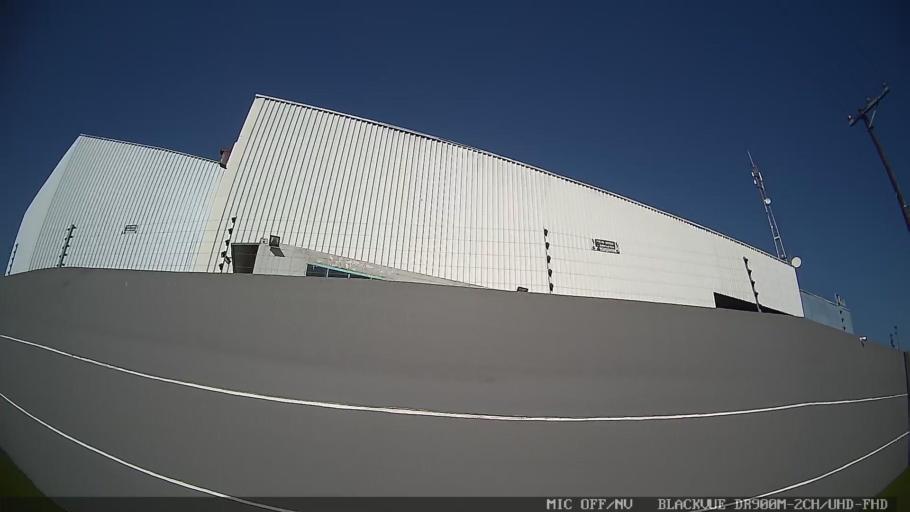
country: BR
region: Sao Paulo
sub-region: Guaruja
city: Guaruja
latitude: -24.0040
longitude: -46.2920
